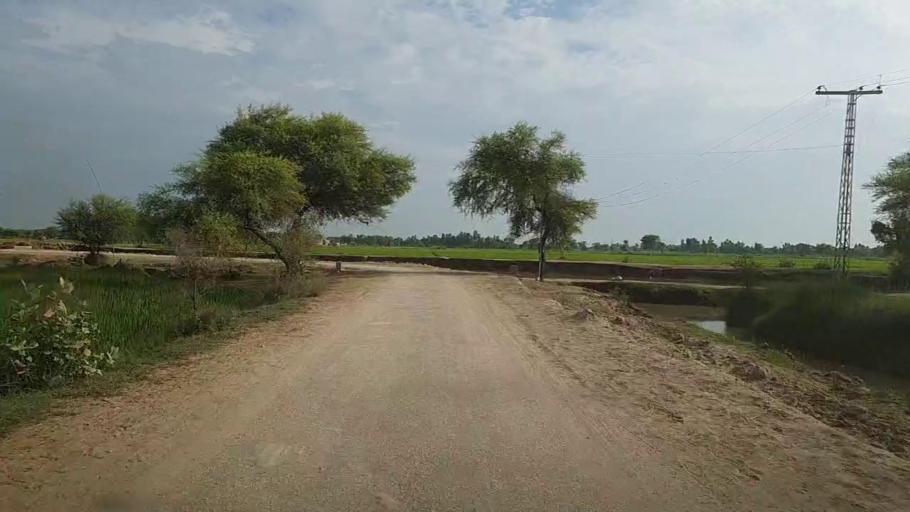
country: PK
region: Sindh
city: Thul
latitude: 28.2548
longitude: 68.8577
